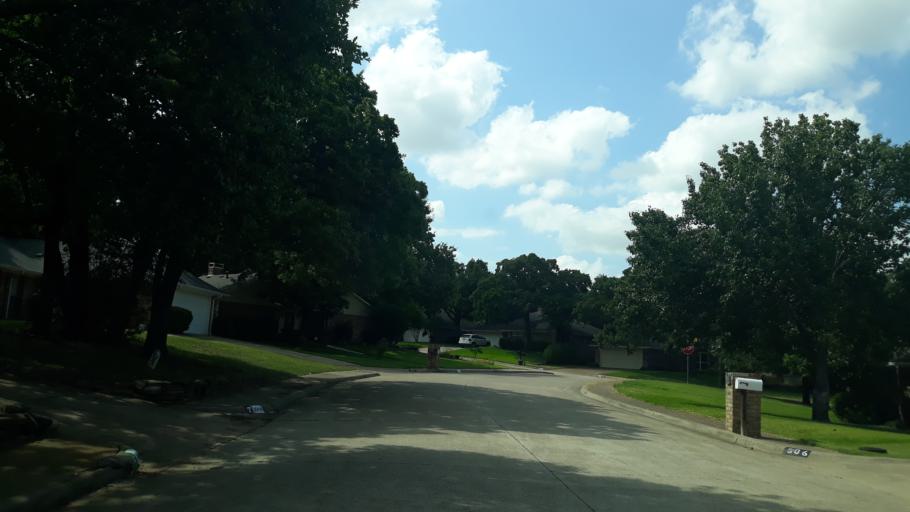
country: US
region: Texas
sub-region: Dallas County
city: Irving
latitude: 32.8133
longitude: -96.9972
